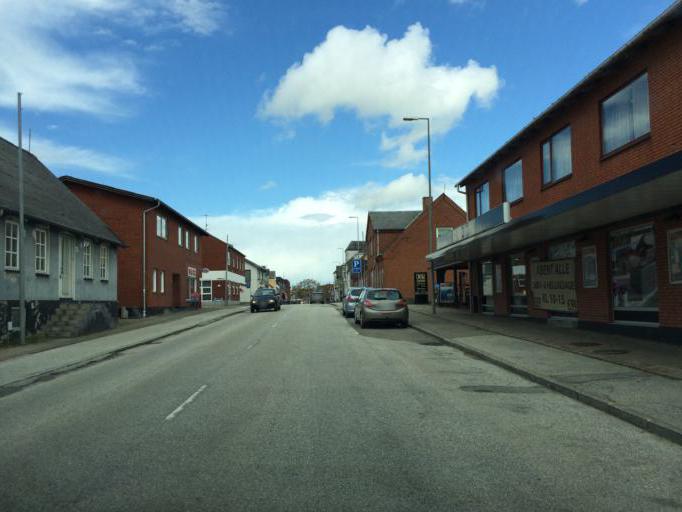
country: DK
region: North Denmark
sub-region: Vesthimmerland Kommune
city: Farso
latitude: 56.7696
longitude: 9.3403
